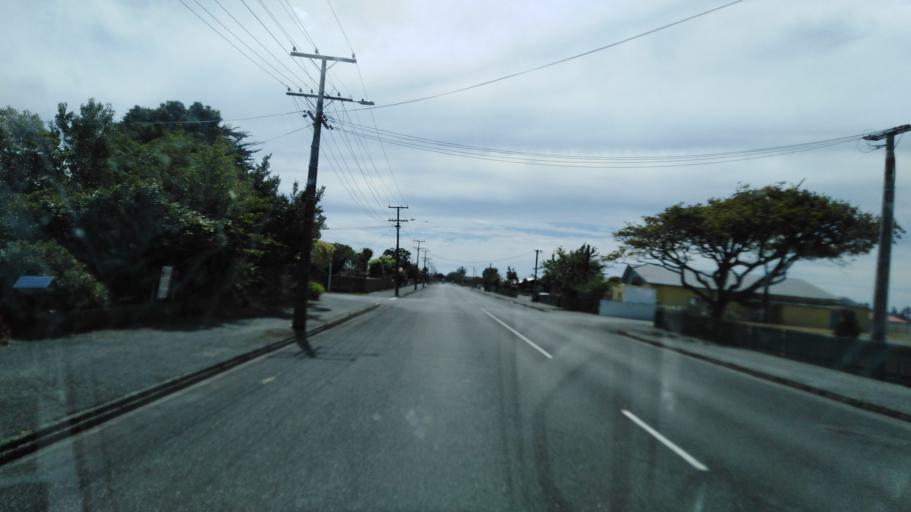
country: NZ
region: West Coast
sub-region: Buller District
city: Westport
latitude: -41.7458
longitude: 171.6035
